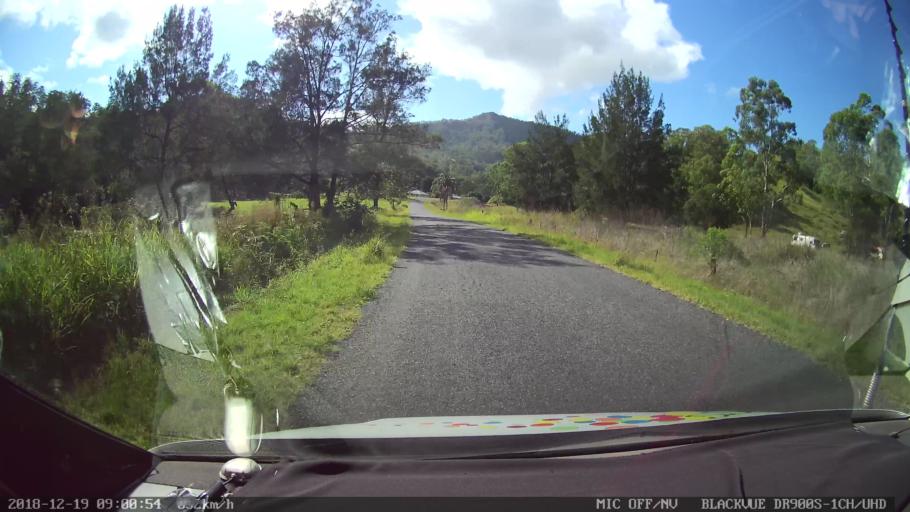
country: AU
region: New South Wales
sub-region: Kyogle
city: Kyogle
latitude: -28.4354
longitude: 152.9575
